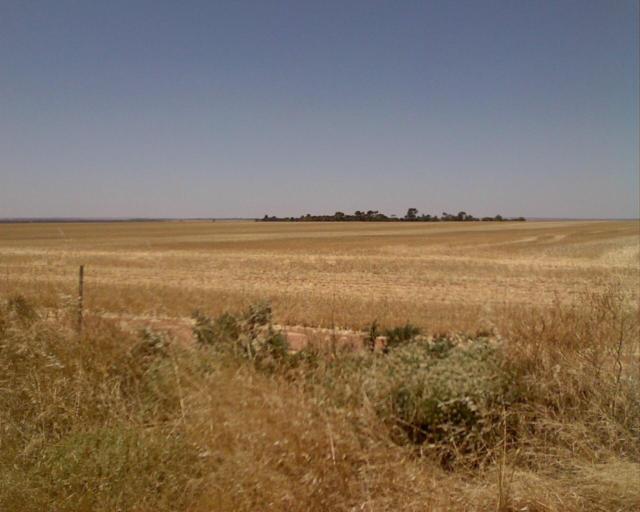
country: AU
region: Western Australia
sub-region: Wongan-Ballidu
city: Wongan Hills
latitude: -30.3668
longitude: 117.1695
